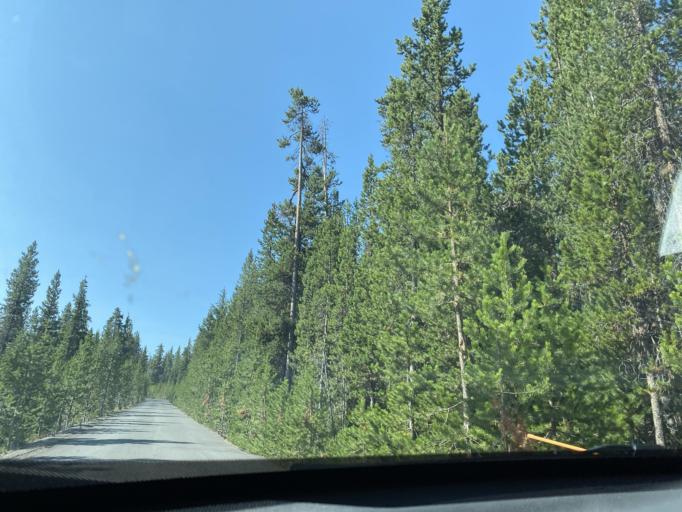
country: US
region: Oregon
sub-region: Deschutes County
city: Three Rivers
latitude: 43.7086
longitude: -121.2746
